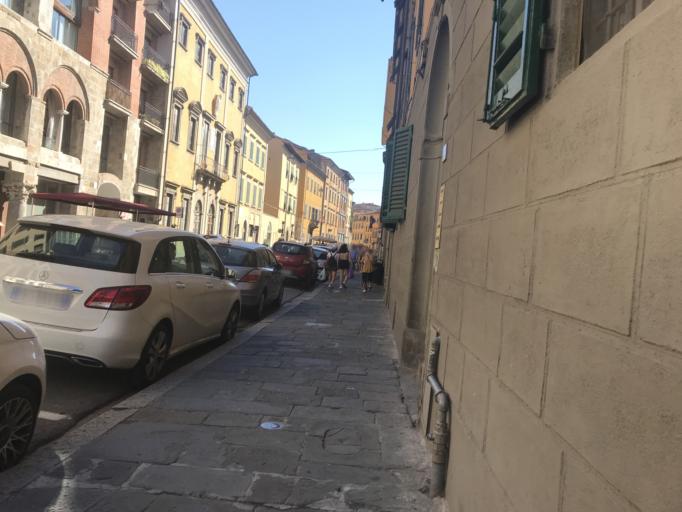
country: IT
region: Tuscany
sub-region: Province of Pisa
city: Pisa
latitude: 43.7189
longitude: 10.3973
